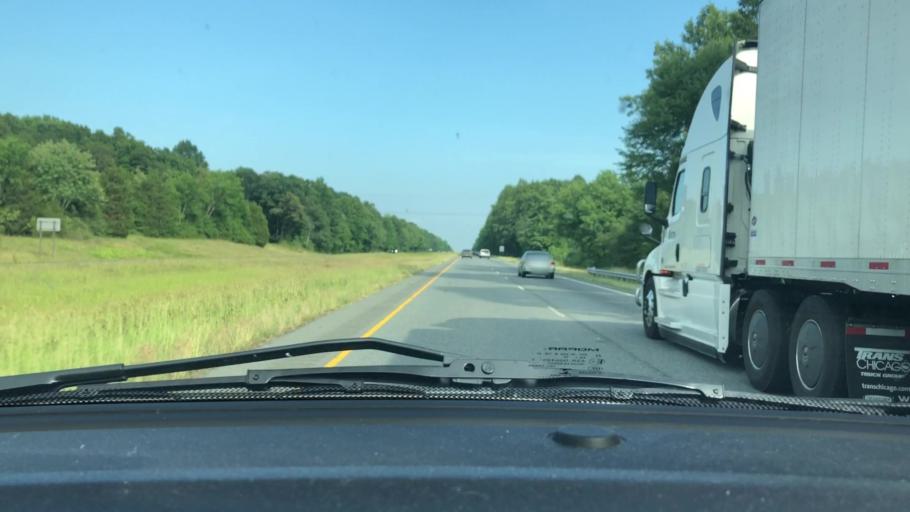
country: US
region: North Carolina
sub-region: Randolph County
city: Liberty
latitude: 35.8414
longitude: -79.5984
